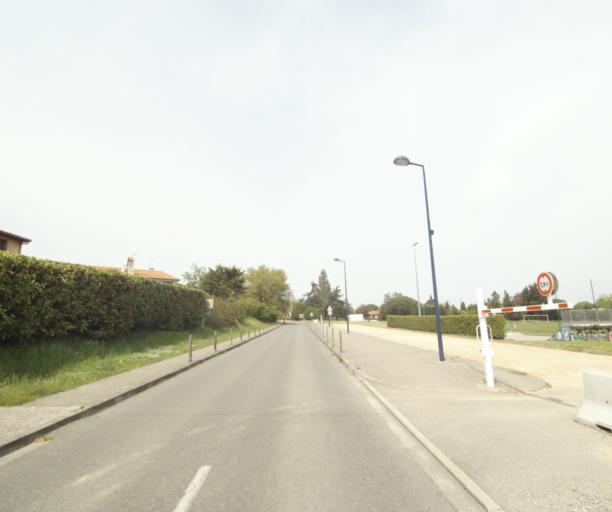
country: FR
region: Midi-Pyrenees
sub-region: Departement de la Haute-Garonne
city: Auzeville-Tolosane
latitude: 43.5232
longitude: 1.4894
